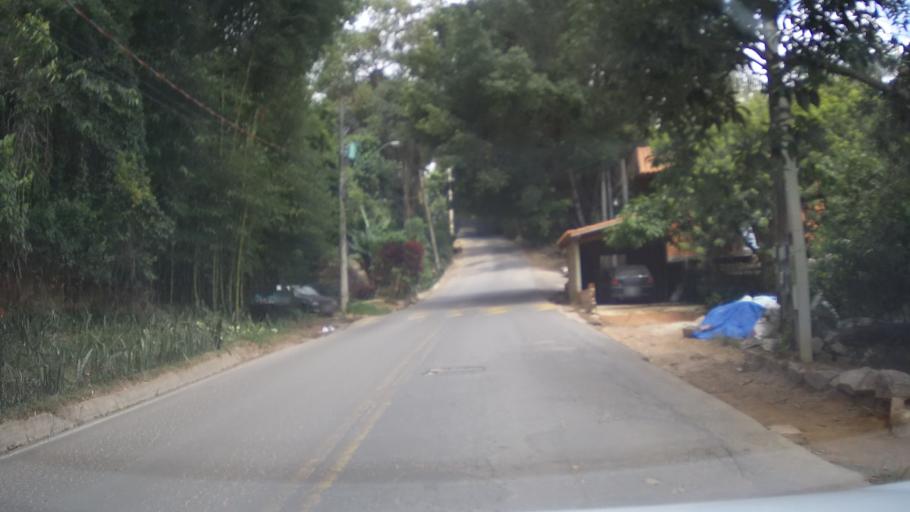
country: BR
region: Sao Paulo
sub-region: Valinhos
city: Valinhos
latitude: -22.9797
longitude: -46.9490
